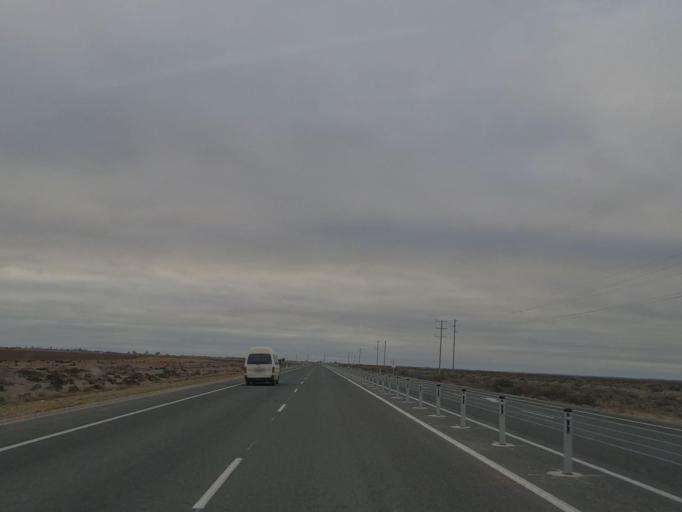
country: AU
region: Victoria
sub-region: Swan Hill
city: Swan Hill
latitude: -35.5146
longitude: 143.7271
